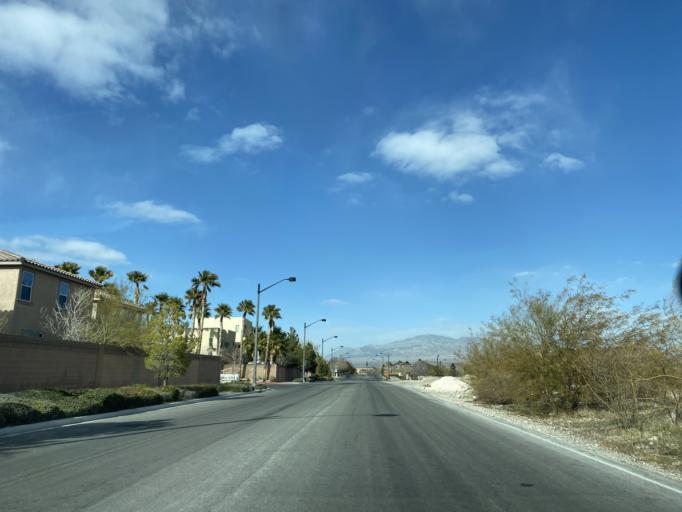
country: US
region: Nevada
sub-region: Clark County
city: Summerlin South
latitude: 36.3051
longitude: -115.3013
